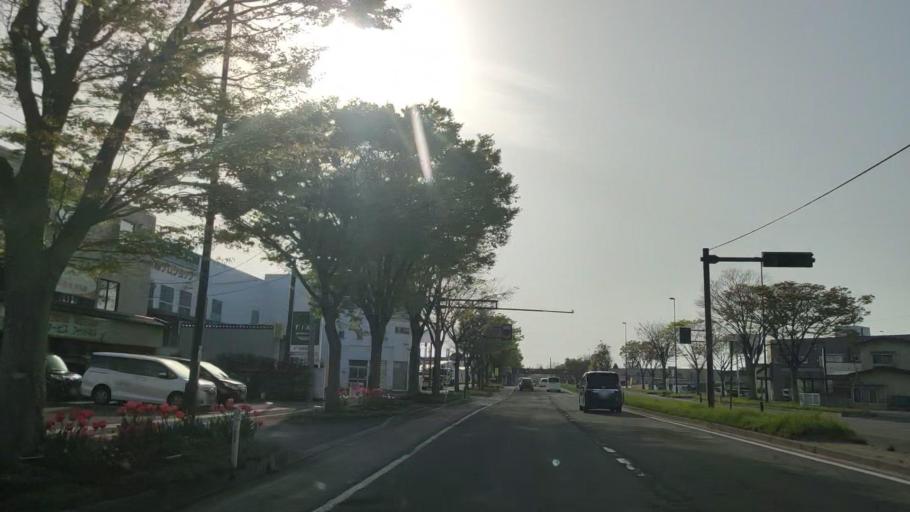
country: JP
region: Aomori
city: Aomori Shi
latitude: 40.8272
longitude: 140.7942
